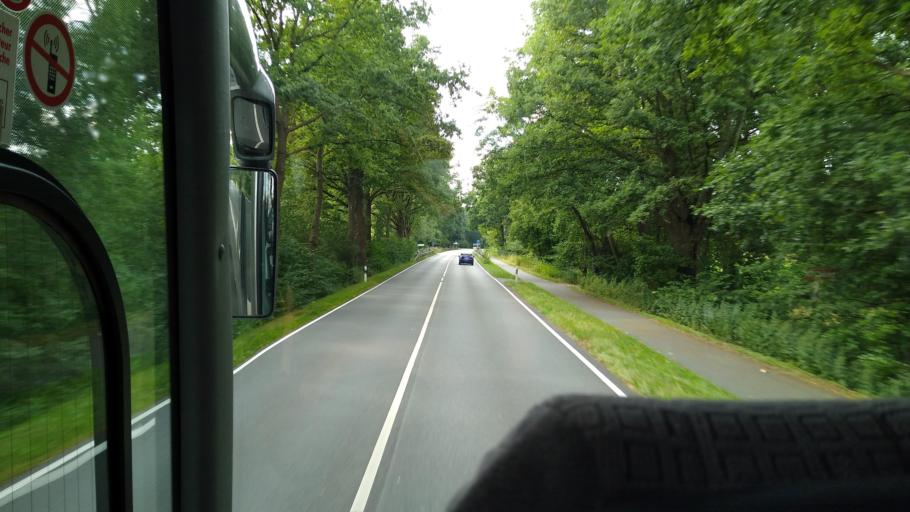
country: DE
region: North Rhine-Westphalia
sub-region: Regierungsbezirk Detmold
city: Hovelhof
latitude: 51.7999
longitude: 8.6819
